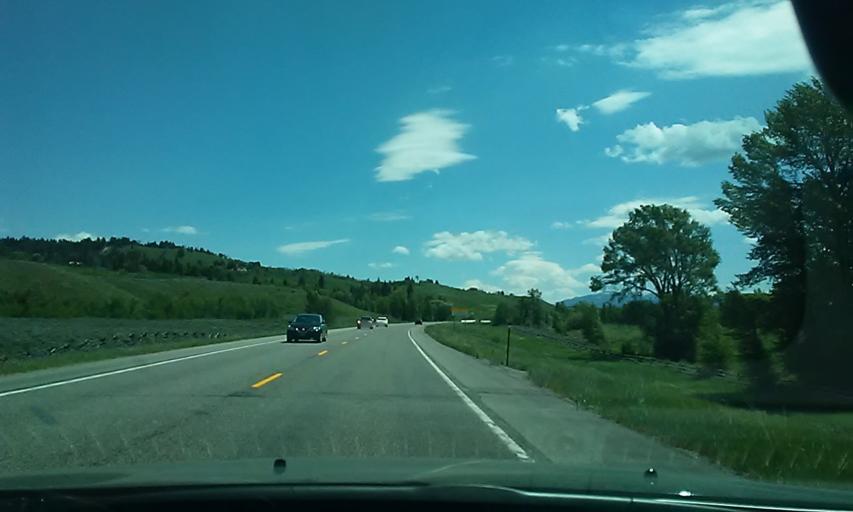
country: US
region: Wyoming
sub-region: Teton County
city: Jackson
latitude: 43.8397
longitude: -110.4639
